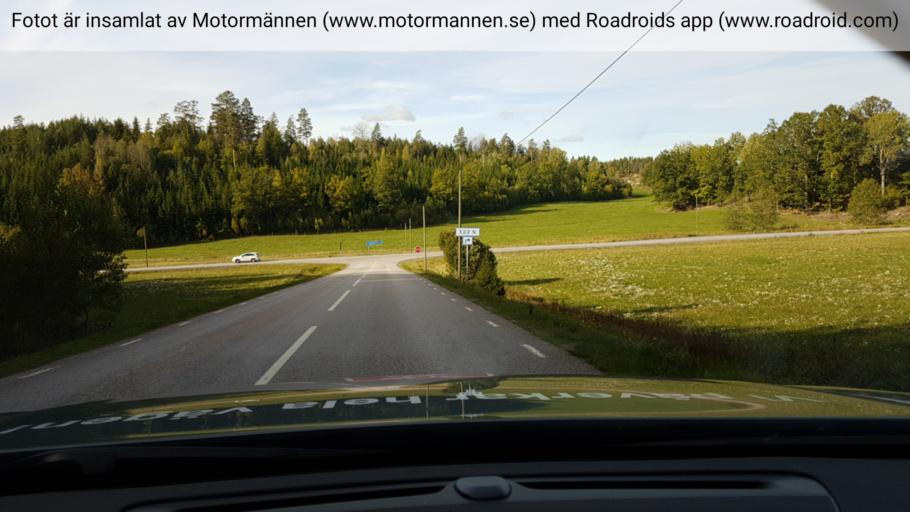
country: SE
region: OEstergoetland
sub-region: Valdemarsviks Kommun
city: Valdemarsvik
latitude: 58.1863
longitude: 16.5854
